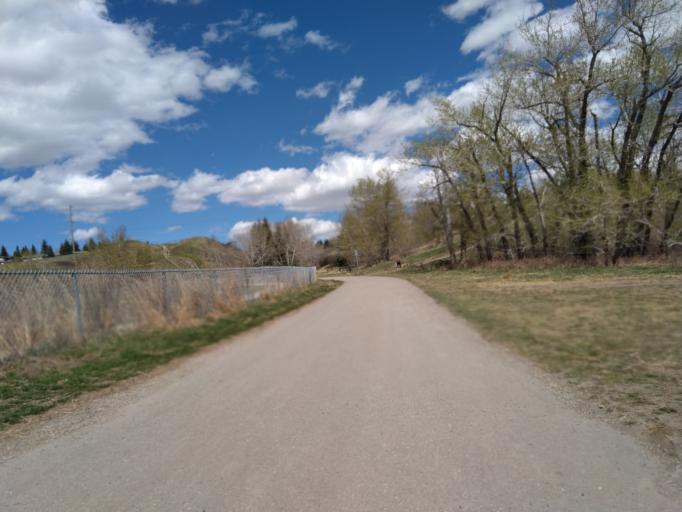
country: CA
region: Alberta
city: Calgary
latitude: 51.1004
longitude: -114.2013
